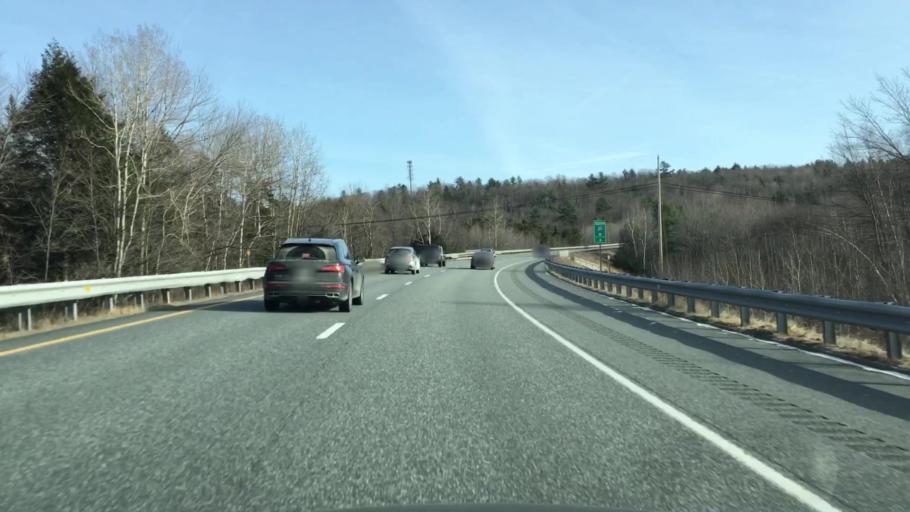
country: US
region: New Hampshire
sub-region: Sullivan County
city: Grantham
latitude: 43.4900
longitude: -72.1121
